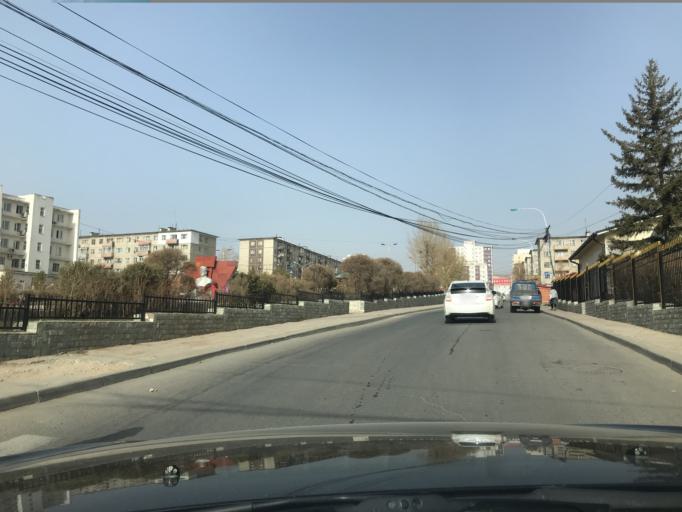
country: MN
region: Ulaanbaatar
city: Ulaanbaatar
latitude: 47.9176
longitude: 106.9530
